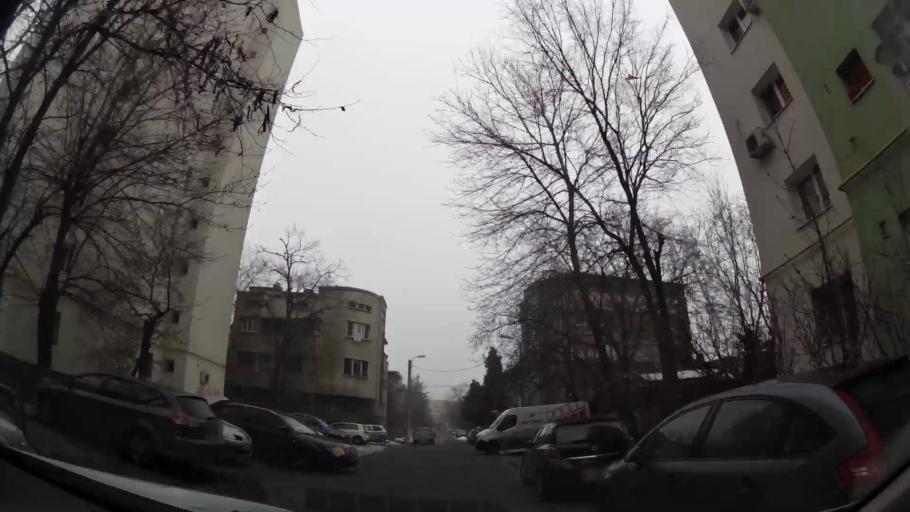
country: RO
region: Bucuresti
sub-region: Municipiul Bucuresti
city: Bucharest
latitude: 44.4278
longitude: 26.1260
